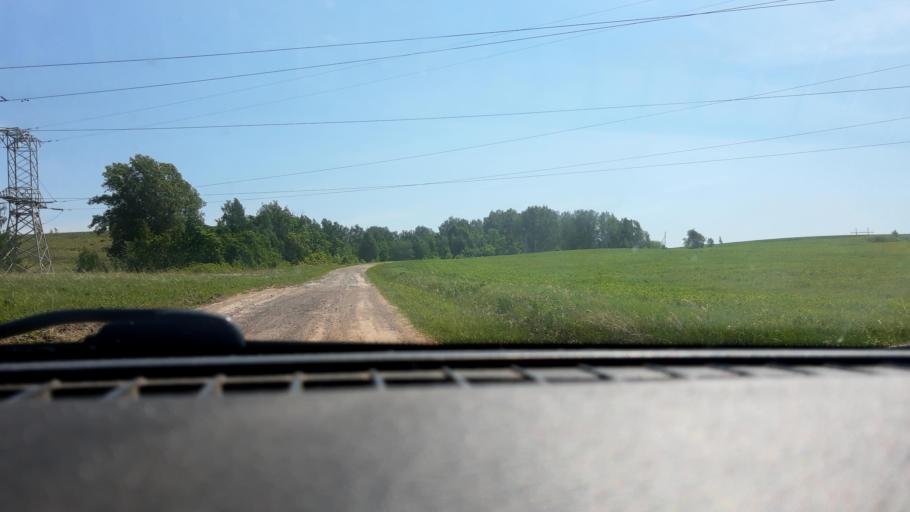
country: RU
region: Bashkortostan
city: Avdon
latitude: 54.4294
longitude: 55.8373
